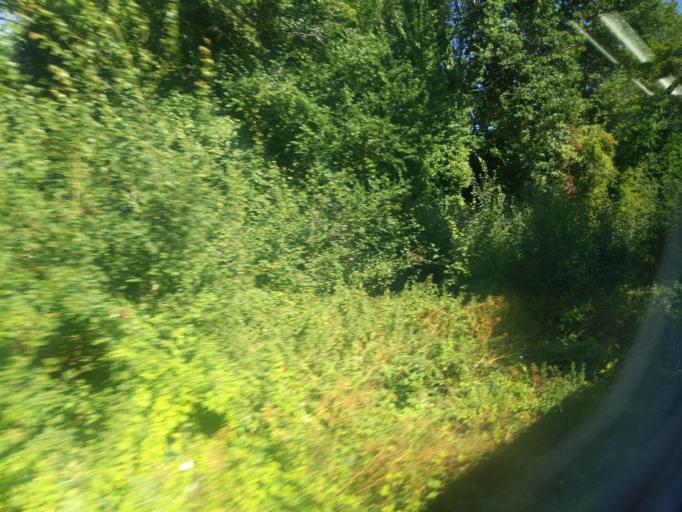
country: GB
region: England
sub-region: Devon
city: Kingskerswell
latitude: 50.4860
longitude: -3.5543
